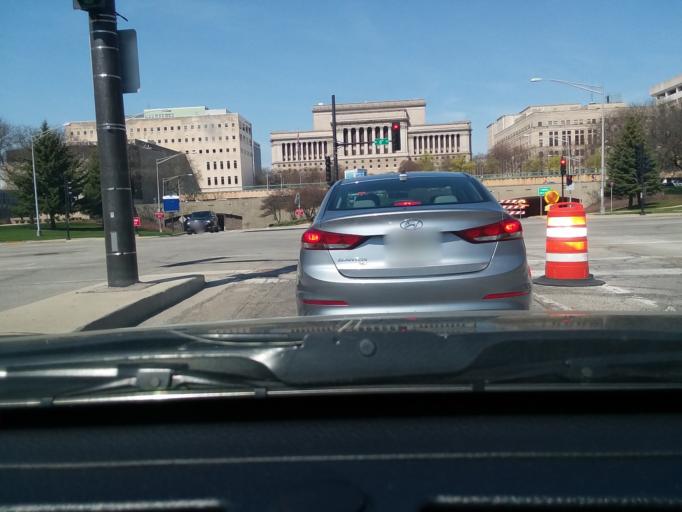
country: US
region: Wisconsin
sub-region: Milwaukee County
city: Milwaukee
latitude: 43.0416
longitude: -87.9186
